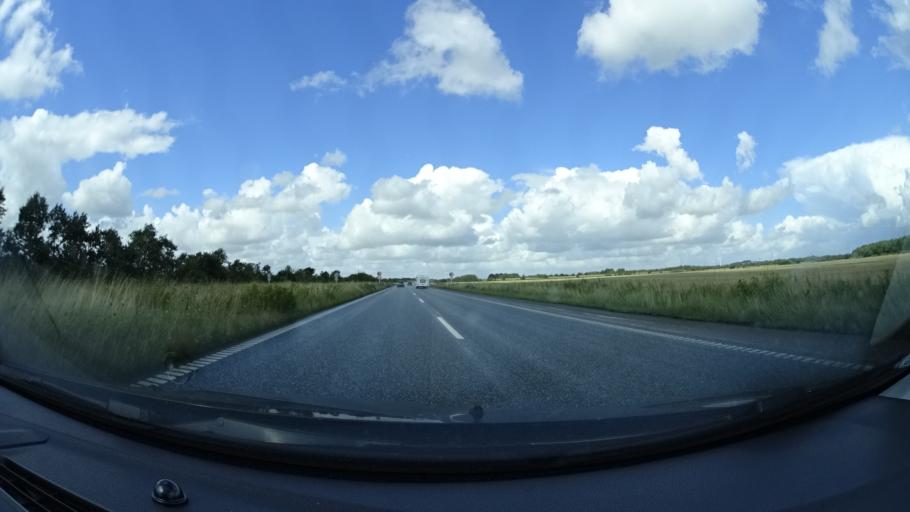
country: DK
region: South Denmark
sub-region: Aabenraa Kommune
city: Krusa
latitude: 54.8911
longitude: 9.3779
